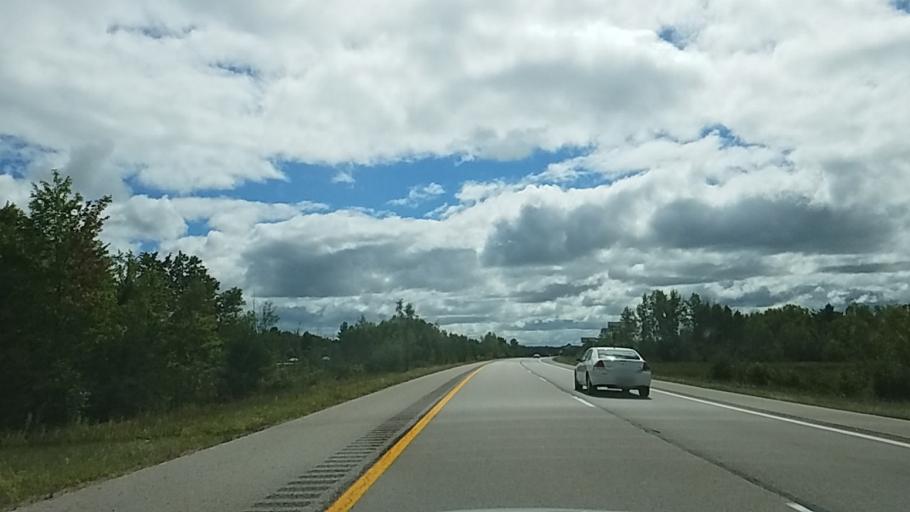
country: US
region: Michigan
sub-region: Ogemaw County
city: Skidway Lake
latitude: 44.0537
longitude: -84.0756
